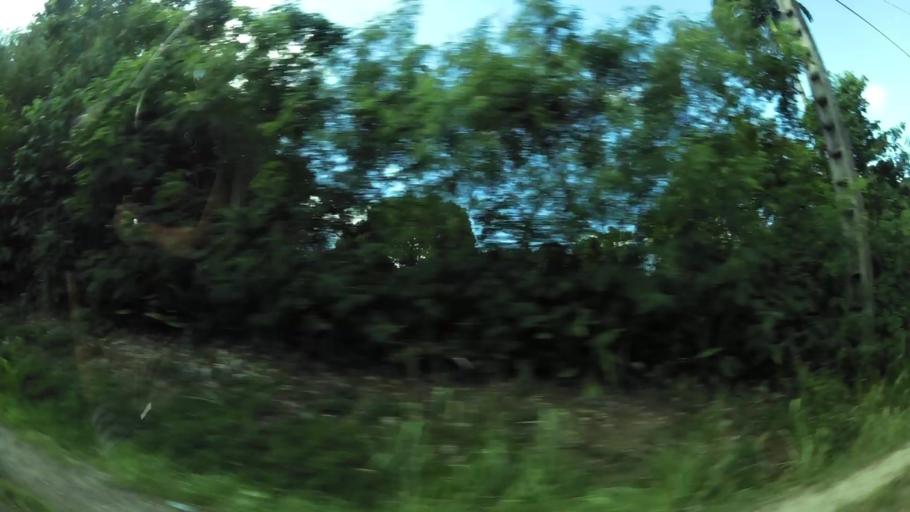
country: GP
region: Guadeloupe
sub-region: Guadeloupe
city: Petit-Canal
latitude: 16.3728
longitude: -61.4527
